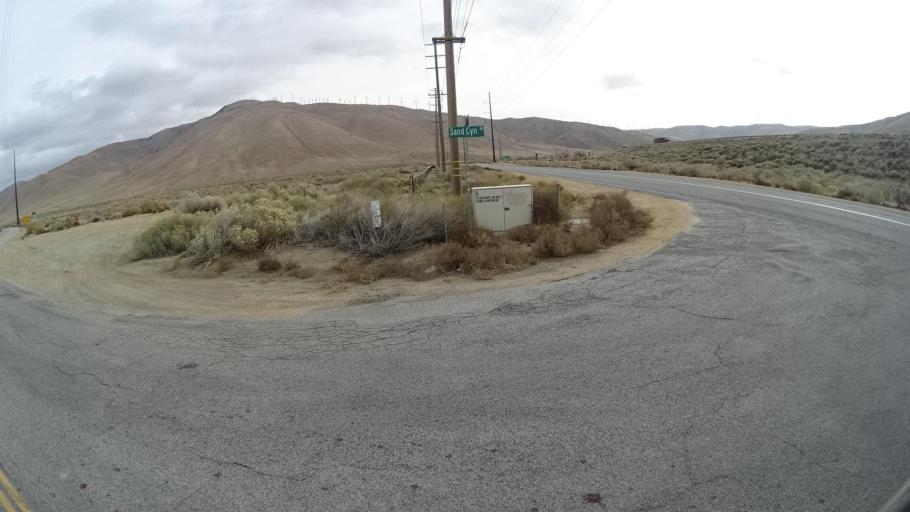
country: US
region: California
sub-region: Kern County
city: Tehachapi
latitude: 35.1115
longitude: -118.3252
